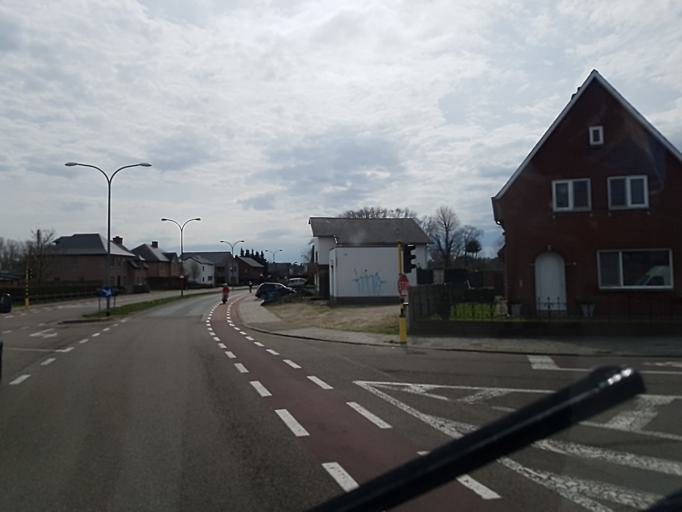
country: BE
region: Flanders
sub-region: Provincie Limburg
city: Overpelt
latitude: 51.2136
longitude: 5.4319
